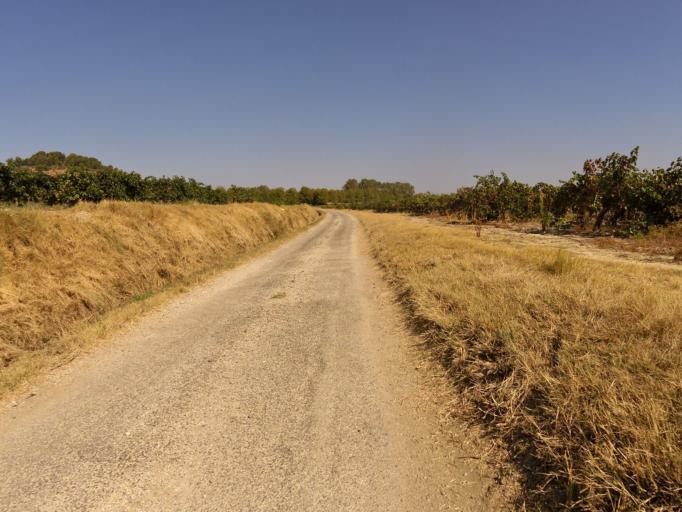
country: FR
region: Languedoc-Roussillon
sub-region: Departement du Gard
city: Calvisson
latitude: 43.7753
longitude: 4.1919
